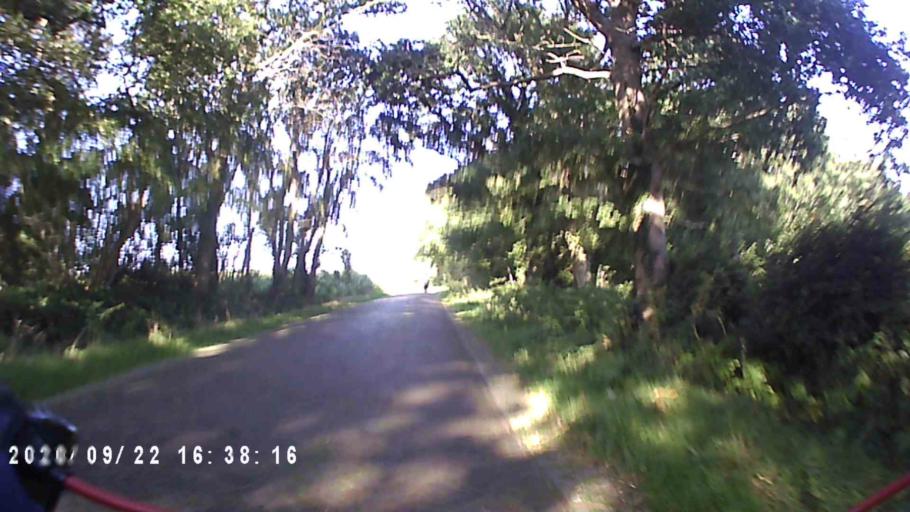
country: NL
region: Groningen
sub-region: Gemeente Leek
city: Leek
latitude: 53.1094
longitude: 6.4461
